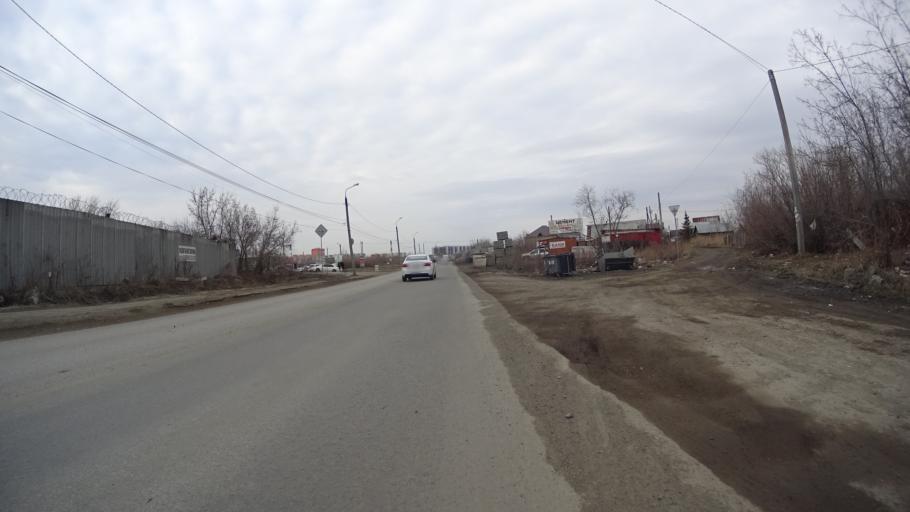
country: RU
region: Chelyabinsk
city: Zheleznodorozhnyy
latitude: 55.1609
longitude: 61.5226
